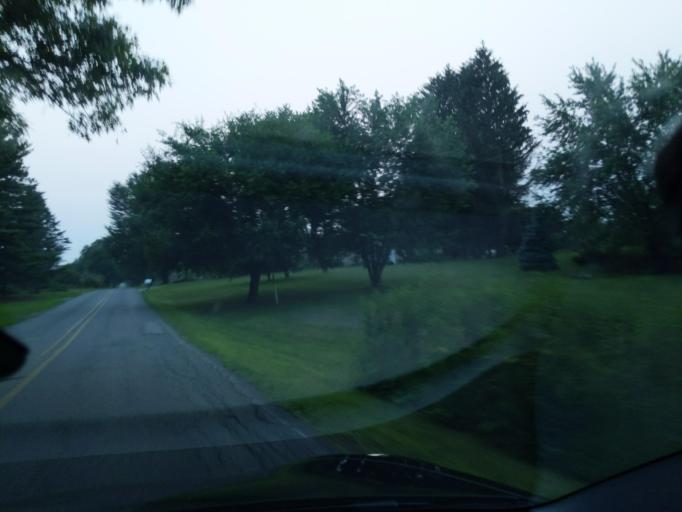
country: US
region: Michigan
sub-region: Ingham County
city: Leslie
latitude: 42.3714
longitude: -84.4953
